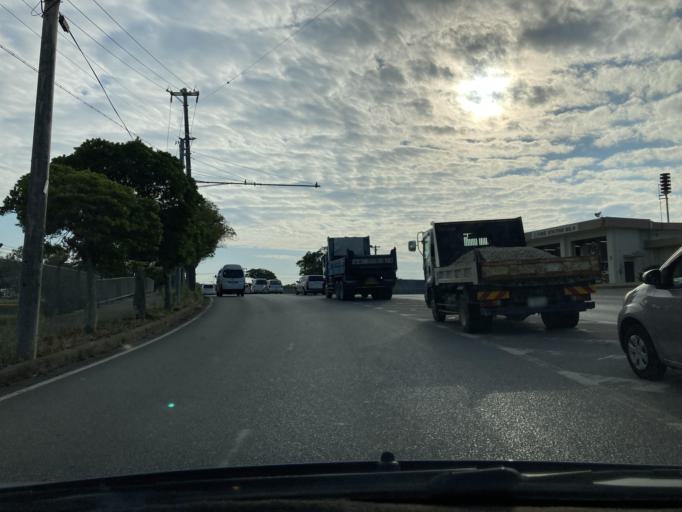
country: JP
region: Okinawa
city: Okinawa
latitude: 26.3637
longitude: 127.7951
